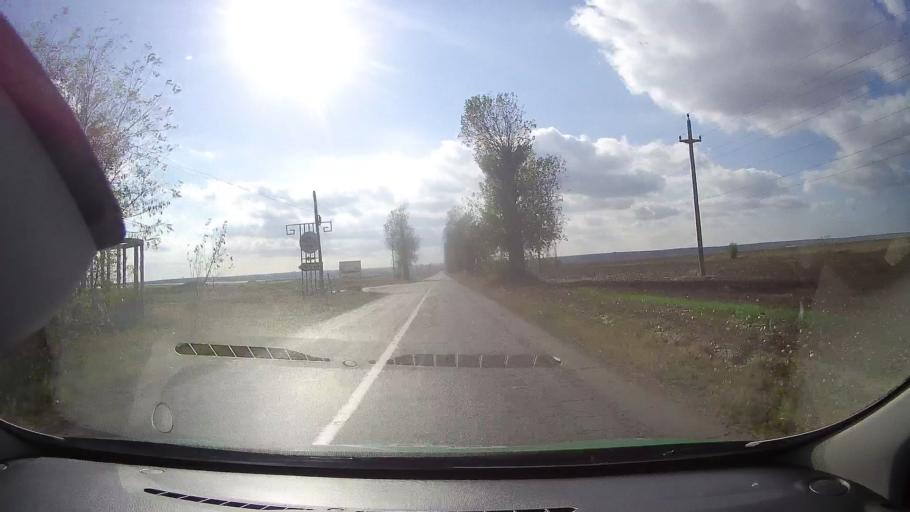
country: RO
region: Constanta
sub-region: Comuna Istria
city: Istria
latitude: 44.5442
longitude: 28.6915
